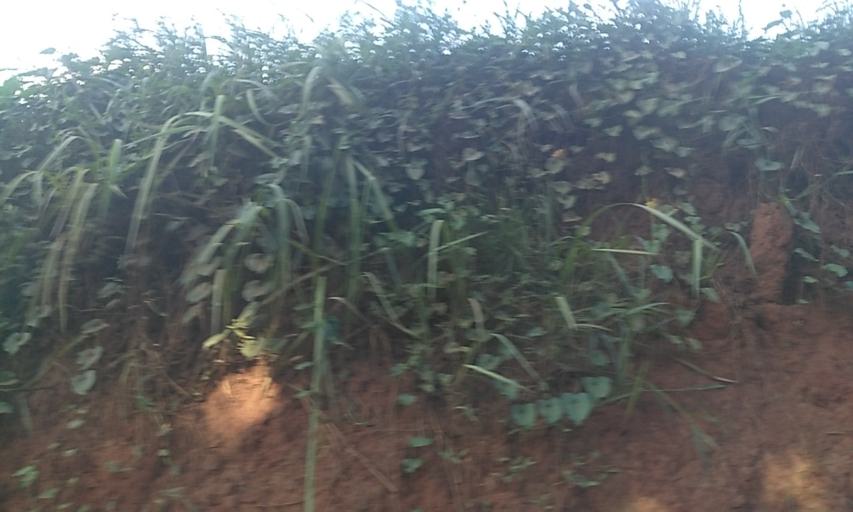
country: UG
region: Central Region
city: Kampala Central Division
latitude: 0.3265
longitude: 32.5370
